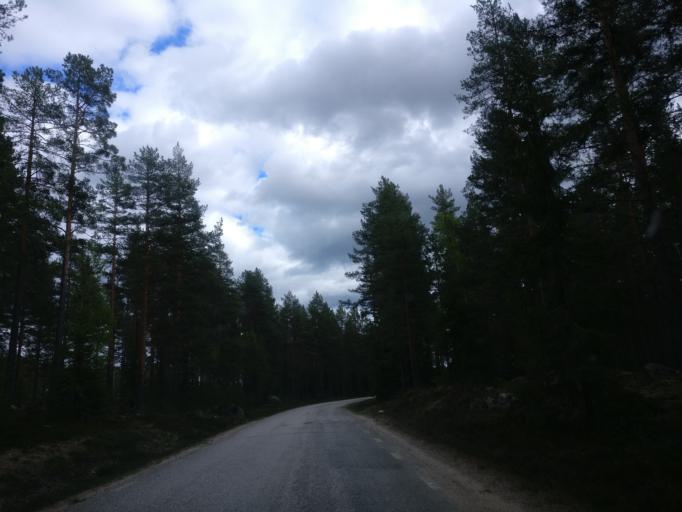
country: SE
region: Gaevleborg
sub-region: Soderhamns Kommun
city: Marielund
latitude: 61.4642
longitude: 17.0855
